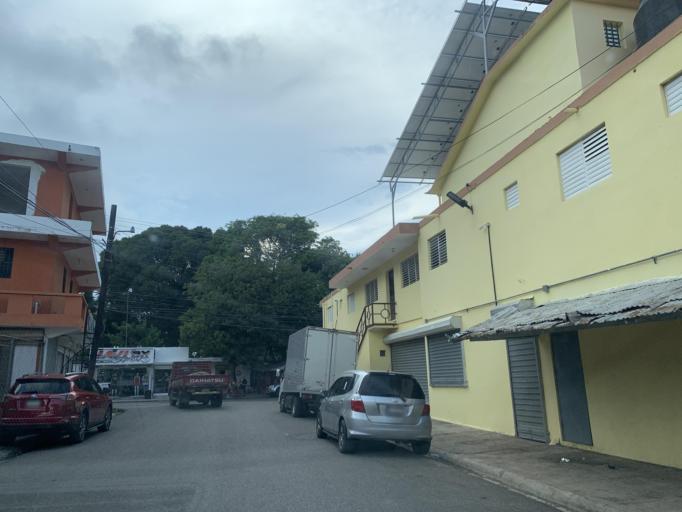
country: DO
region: Puerto Plata
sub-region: Puerto Plata
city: Puerto Plata
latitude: 19.7901
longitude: -70.6965
